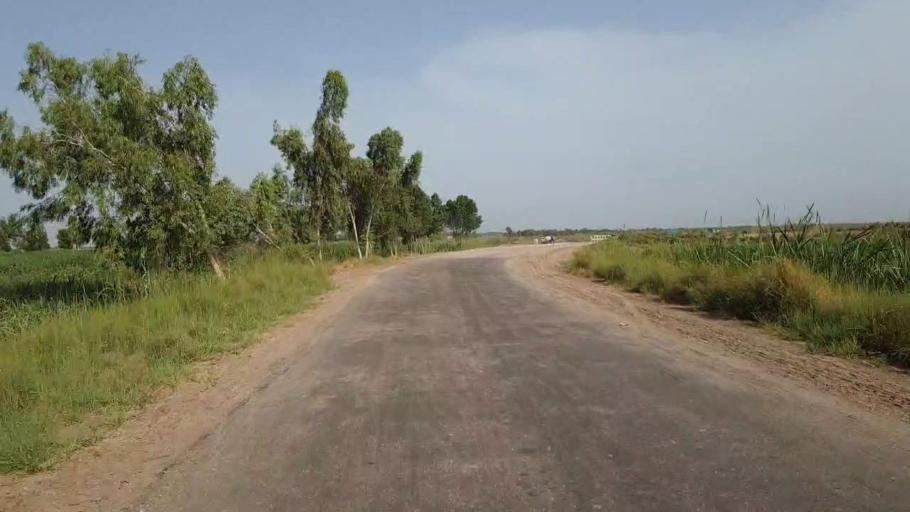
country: PK
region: Sindh
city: Sakrand
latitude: 26.2784
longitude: 68.2705
